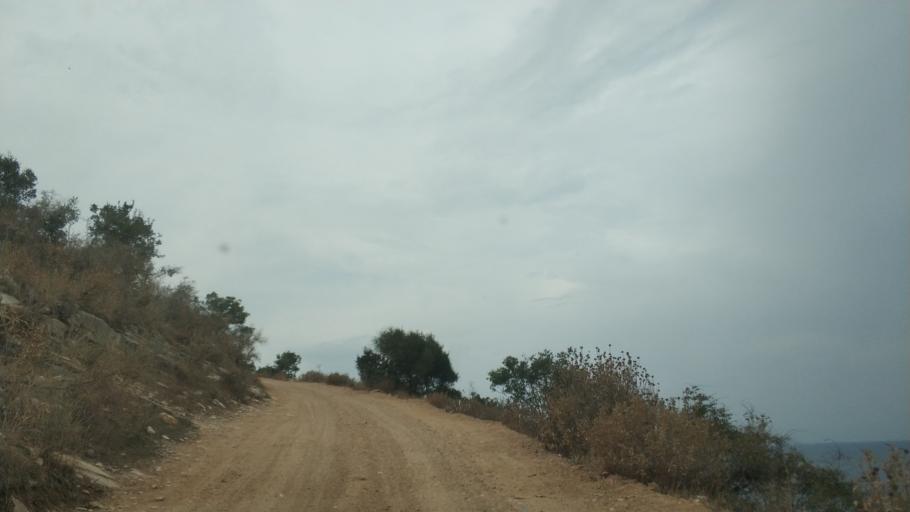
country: AL
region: Vlore
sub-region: Rrethi i Sarandes
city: Sarande
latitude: 39.8000
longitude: 20.0023
